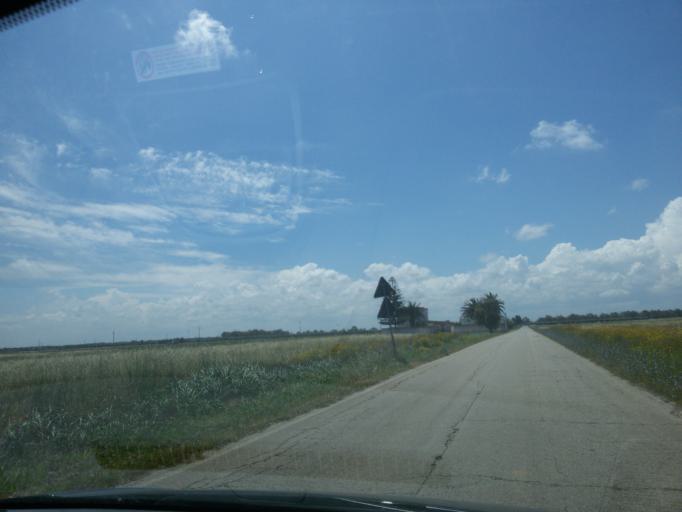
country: IT
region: Apulia
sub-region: Provincia di Brindisi
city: Brindisi
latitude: 40.6588
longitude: 17.8400
